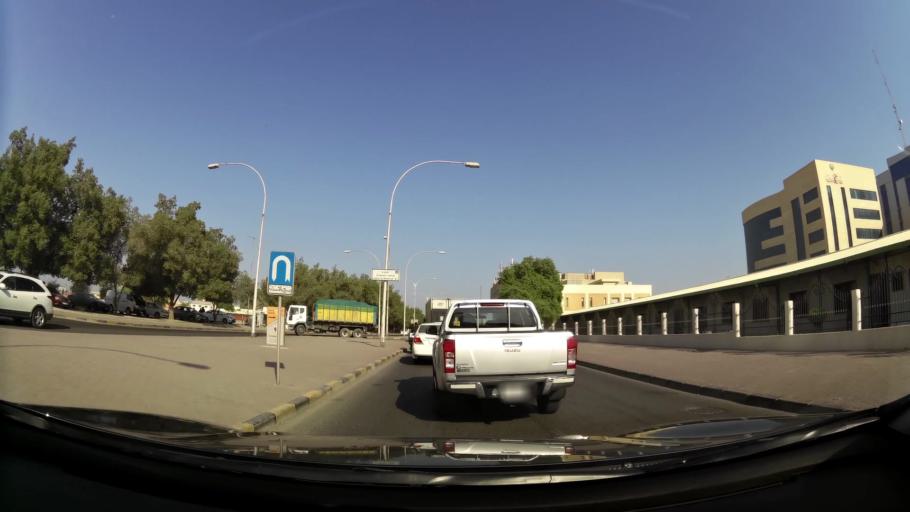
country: KW
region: Al Asimah
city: Kuwait City
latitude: 29.3867
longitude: 47.9867
